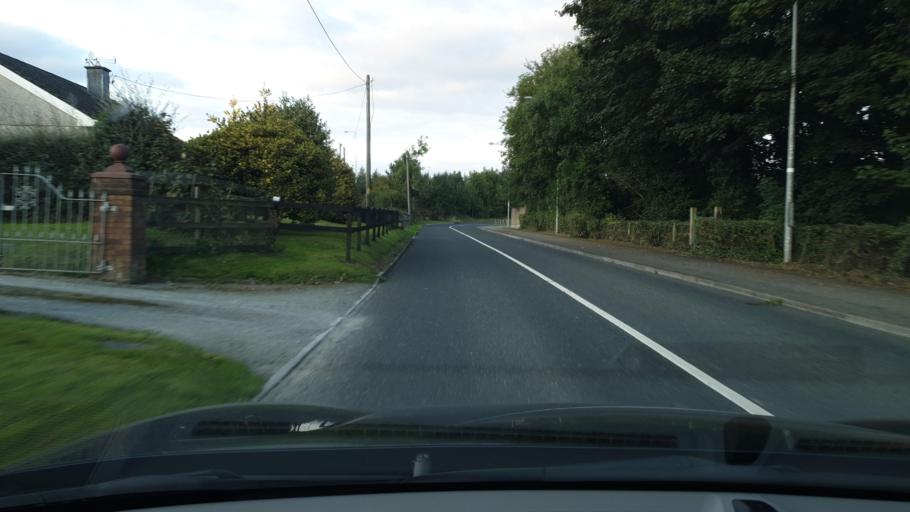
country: IE
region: Leinster
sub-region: Kildare
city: Kill
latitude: 53.2545
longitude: -6.5628
